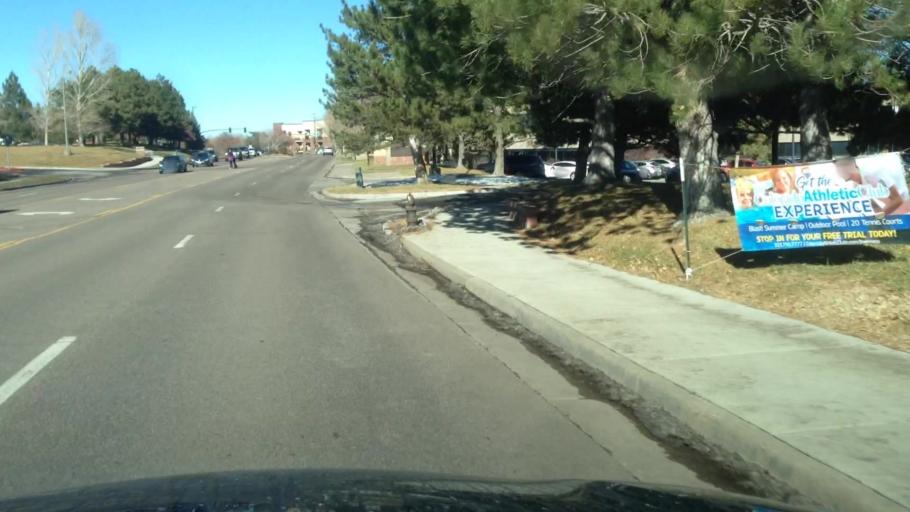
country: US
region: Colorado
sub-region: Douglas County
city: Meridian
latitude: 39.5626
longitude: -104.8655
